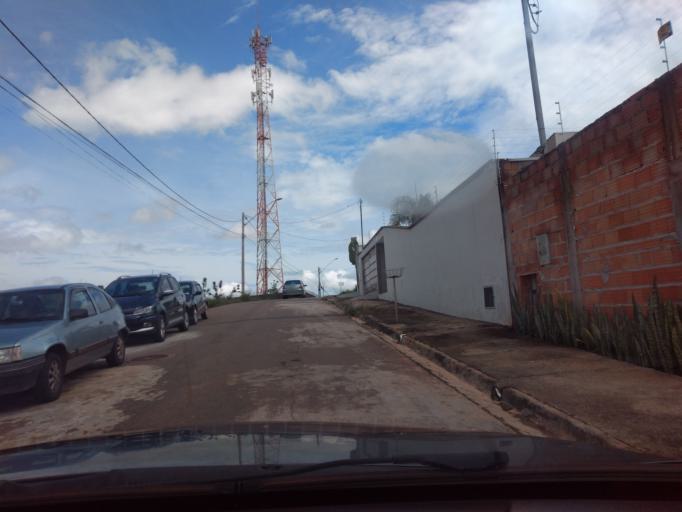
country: BR
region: Minas Gerais
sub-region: Tres Coracoes
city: Tres Coracoes
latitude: -21.6701
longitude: -45.2773
